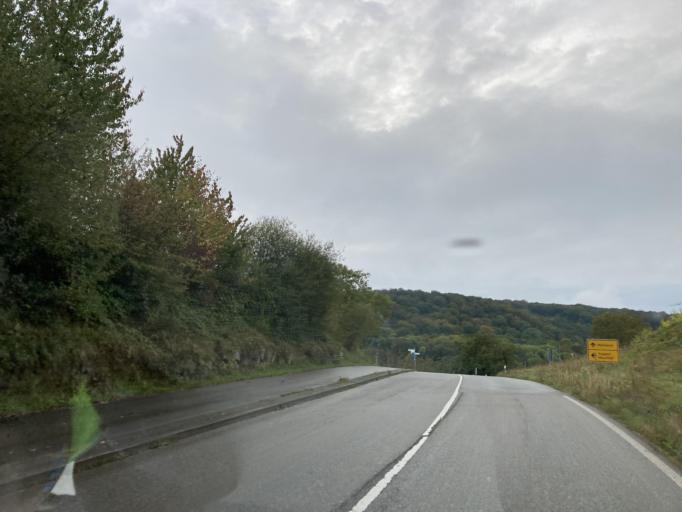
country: DE
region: Baden-Wuerttemberg
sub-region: Freiburg Region
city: Feldberg
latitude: 47.7753
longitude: 7.6224
